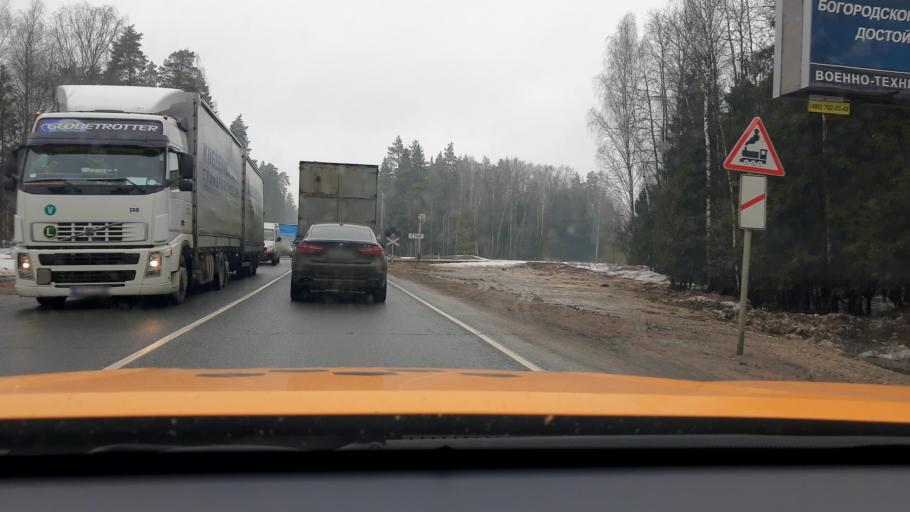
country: RU
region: Moskovskaya
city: Chernogolovka
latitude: 55.9770
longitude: 38.3489
